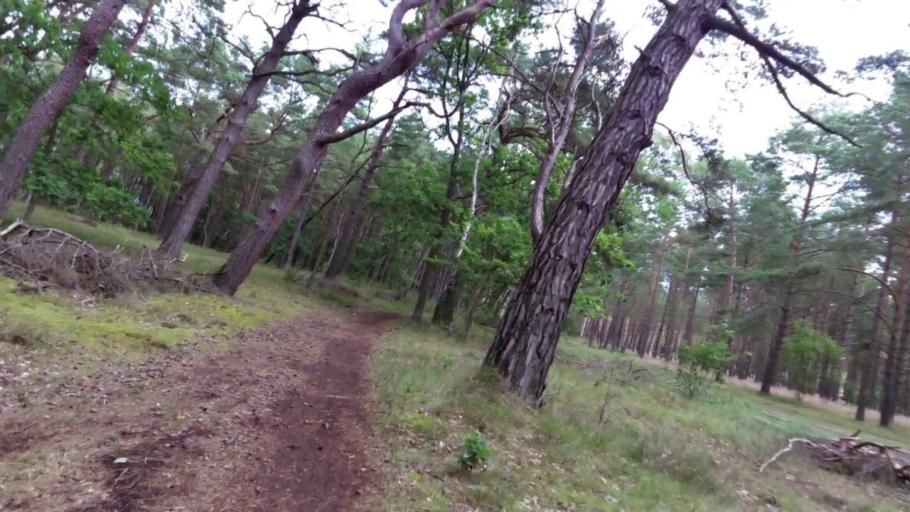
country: PL
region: West Pomeranian Voivodeship
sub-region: Powiat slawienski
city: Darlowo
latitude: 54.5013
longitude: 16.4563
